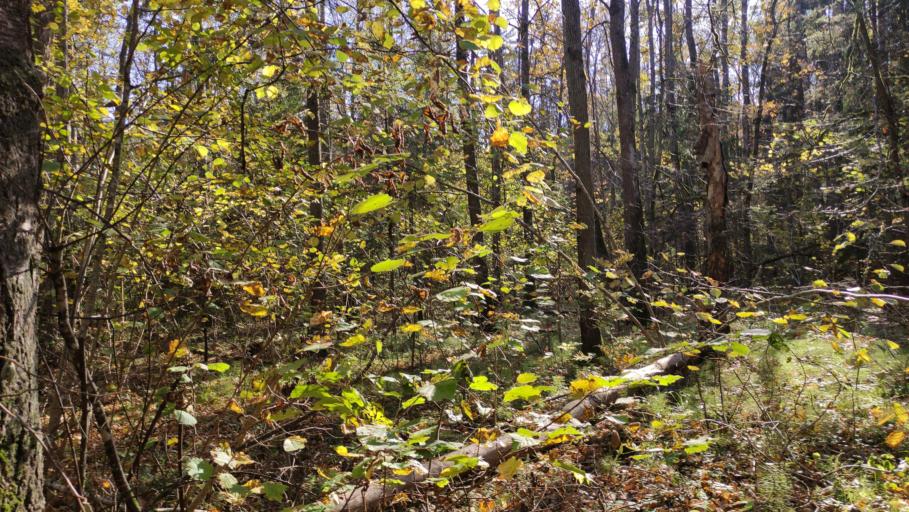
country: LT
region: Alytaus apskritis
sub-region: Alytus
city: Alytus
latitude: 54.3755
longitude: 24.0872
